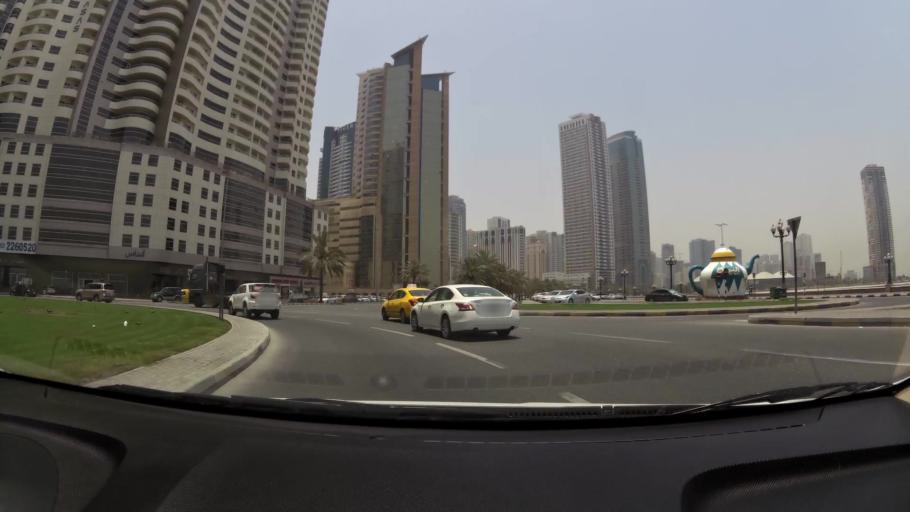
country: AE
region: Ash Shariqah
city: Sharjah
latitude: 25.3184
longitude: 55.3739
